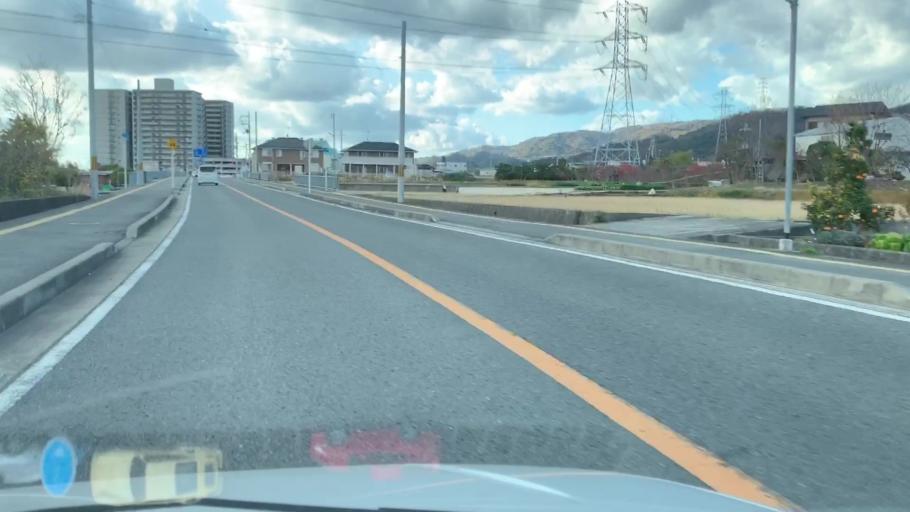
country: JP
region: Wakayama
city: Iwade
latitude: 34.2725
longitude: 135.2804
